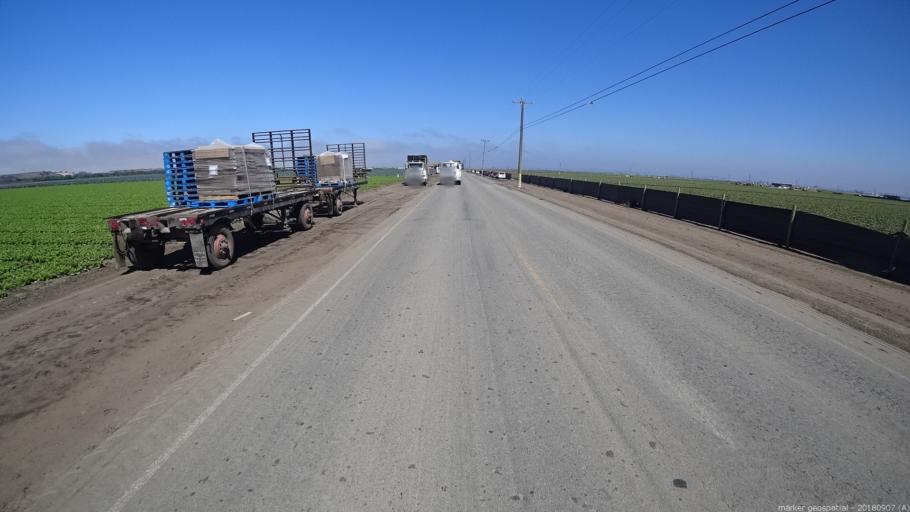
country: US
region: California
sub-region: Monterey County
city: Boronda
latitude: 36.6898
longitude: -121.7350
